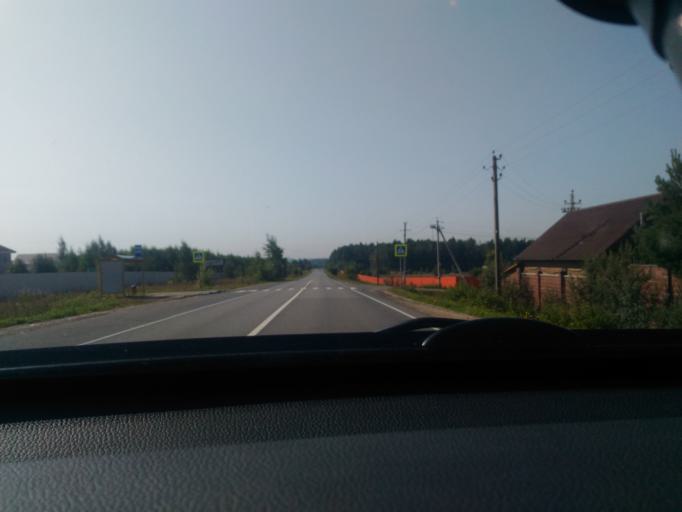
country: RU
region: Moskovskaya
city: Dedenevo
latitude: 56.2538
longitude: 37.5475
